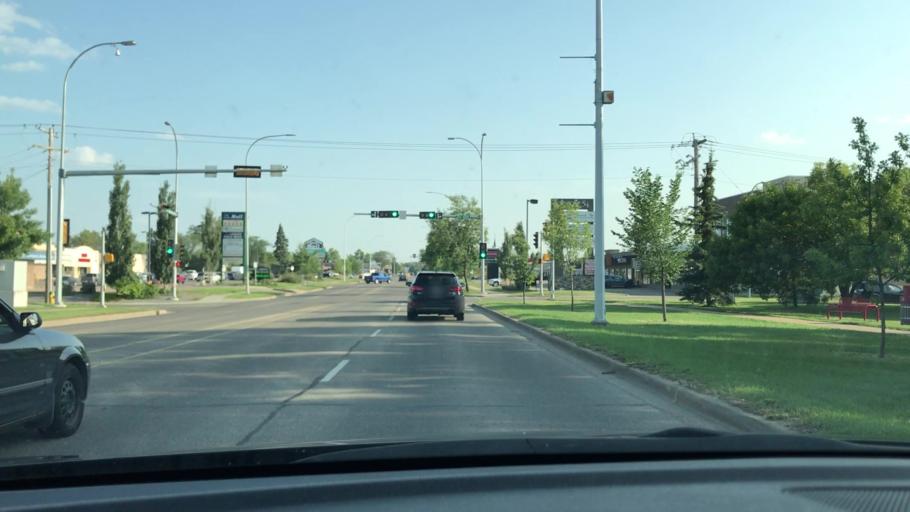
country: CA
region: Alberta
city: Leduc
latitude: 53.2688
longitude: -113.5526
